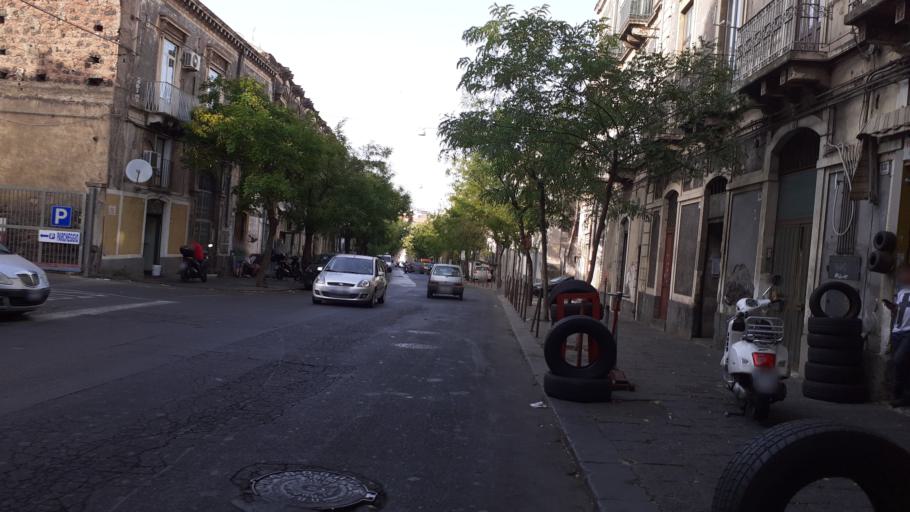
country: IT
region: Sicily
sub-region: Catania
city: Catania
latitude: 37.5053
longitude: 15.0780
